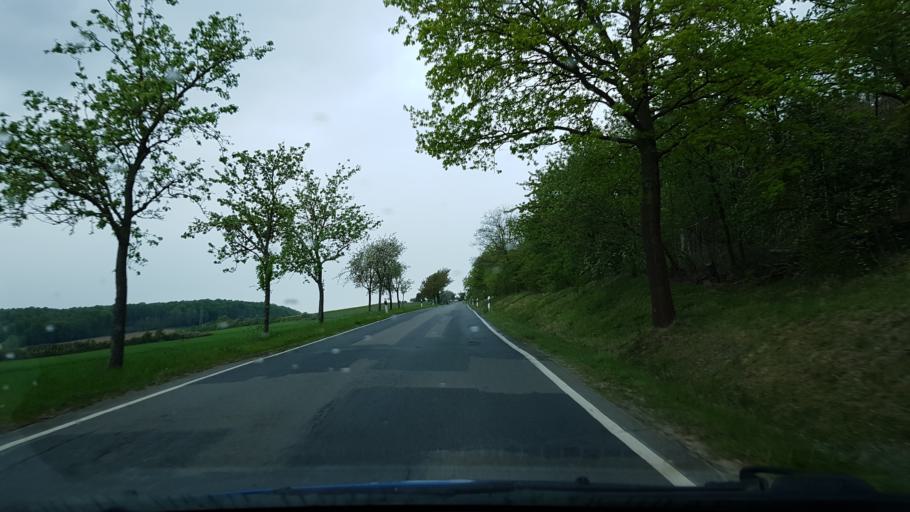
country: DE
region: Lower Saxony
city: Einbeck
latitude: 51.8355
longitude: 9.8289
